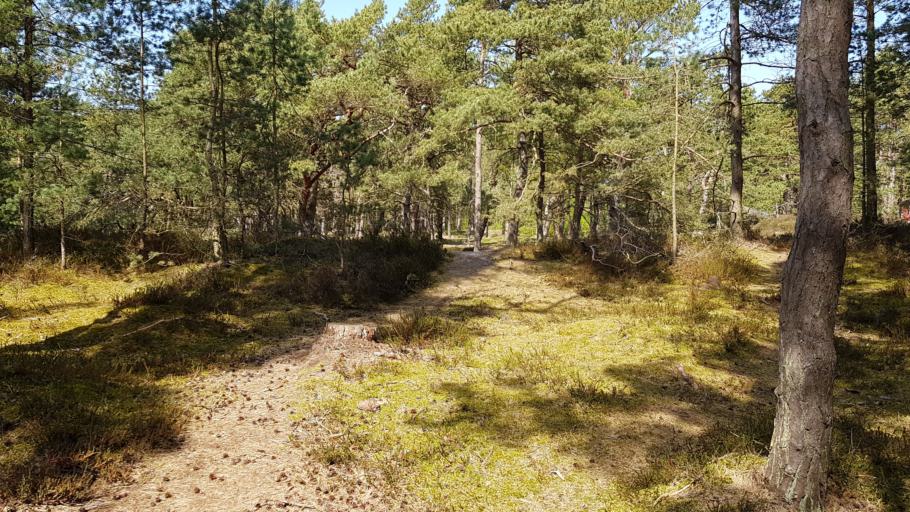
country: DK
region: Capital Region
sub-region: Bornholm Kommune
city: Nexo
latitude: 54.9963
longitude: 15.0852
